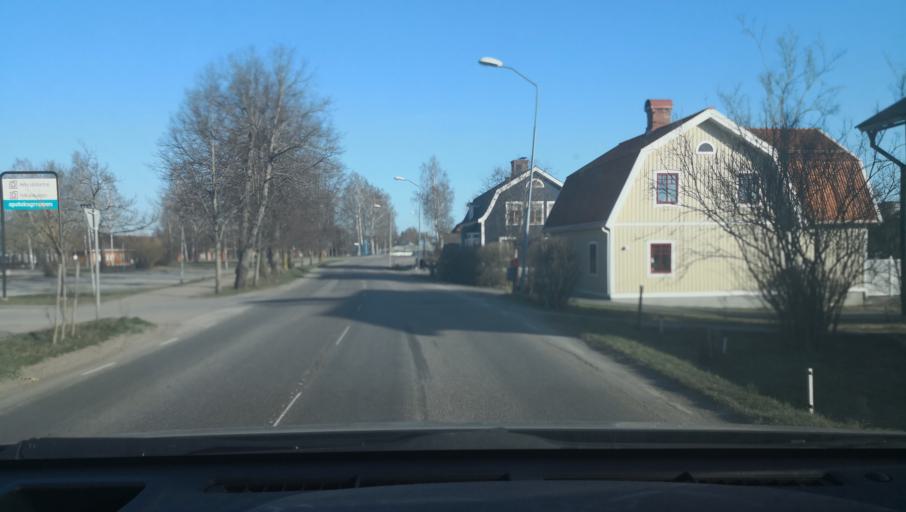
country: SE
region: Uppsala
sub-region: Heby Kommun
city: Heby
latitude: 59.9419
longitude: 16.8608
